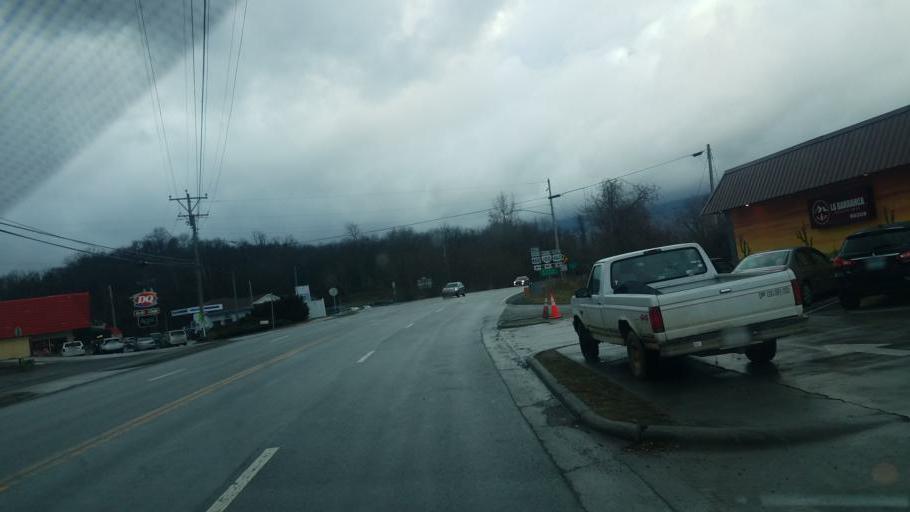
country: US
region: Virginia
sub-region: Giles County
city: Pearisburg
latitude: 37.3303
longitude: -80.7378
